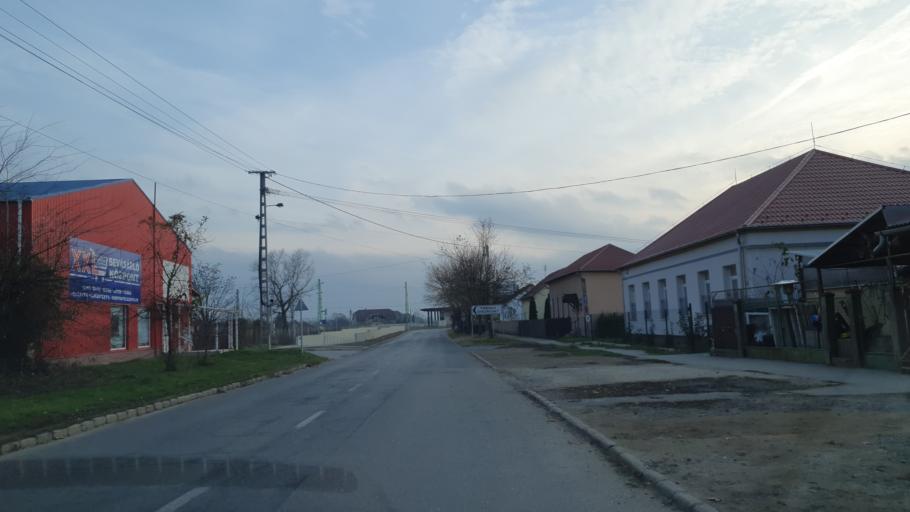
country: HU
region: Szabolcs-Szatmar-Bereg
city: Kisvarda
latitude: 48.2118
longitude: 22.0801
